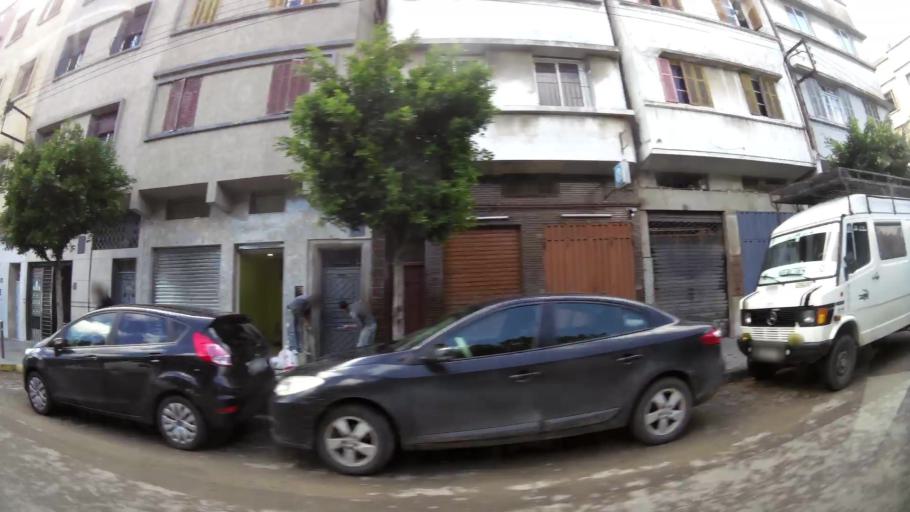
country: MA
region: Grand Casablanca
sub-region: Casablanca
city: Casablanca
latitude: 33.5636
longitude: -7.6111
